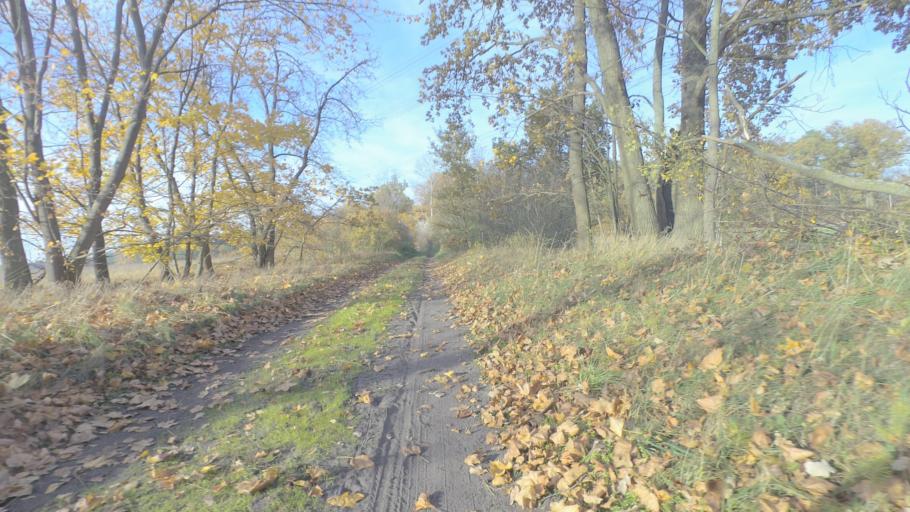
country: DE
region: Brandenburg
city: Trebbin
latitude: 52.2285
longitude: 13.2904
